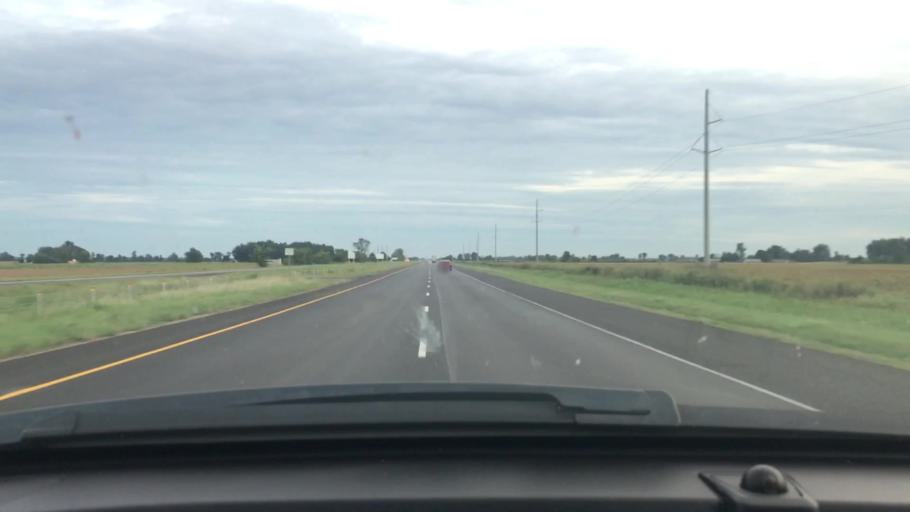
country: US
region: Arkansas
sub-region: Poinsett County
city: Trumann
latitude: 35.6172
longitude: -90.4968
